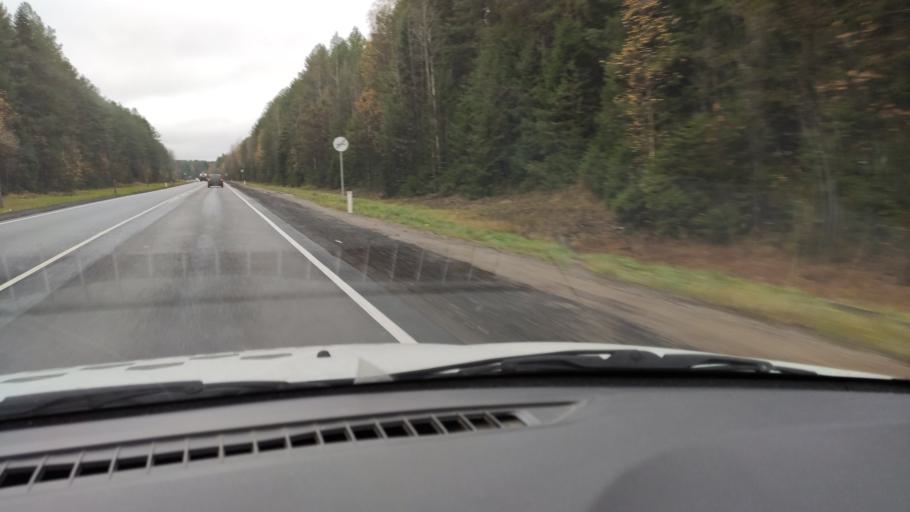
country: RU
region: Kirov
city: Belaya Kholunitsa
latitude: 58.8778
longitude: 50.8674
